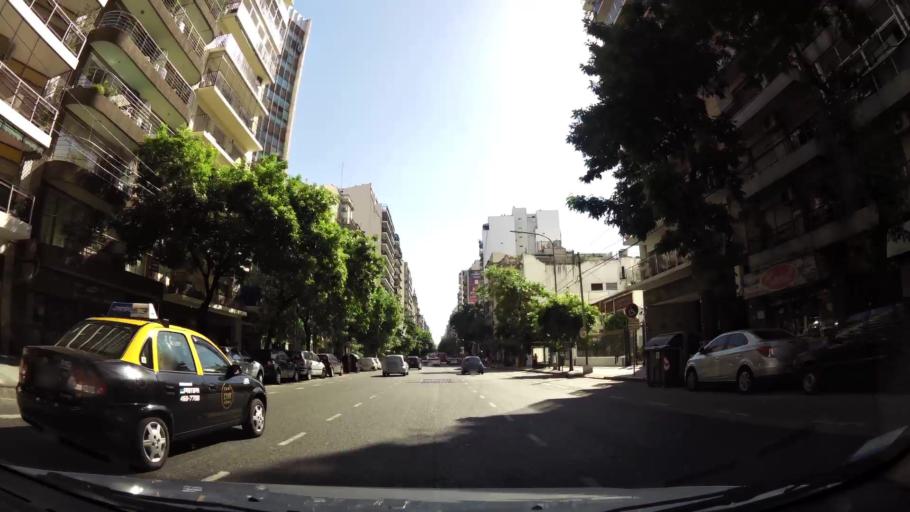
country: AR
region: Buenos Aires F.D.
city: Colegiales
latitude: -34.6134
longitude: -58.4254
